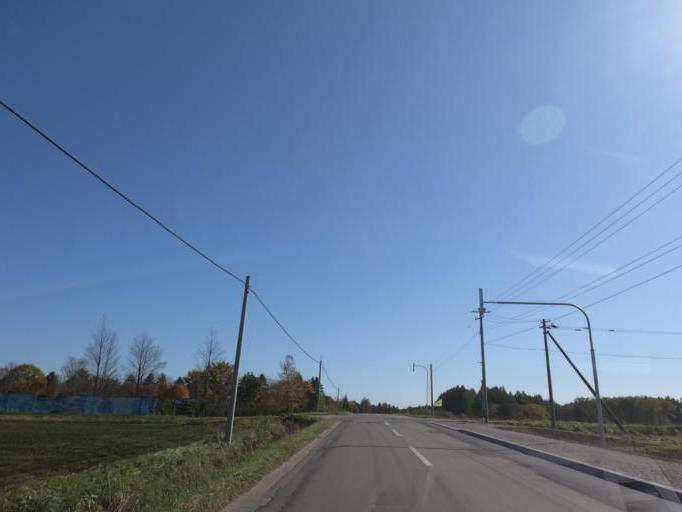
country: JP
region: Hokkaido
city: Obihiro
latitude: 42.8051
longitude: 143.2607
